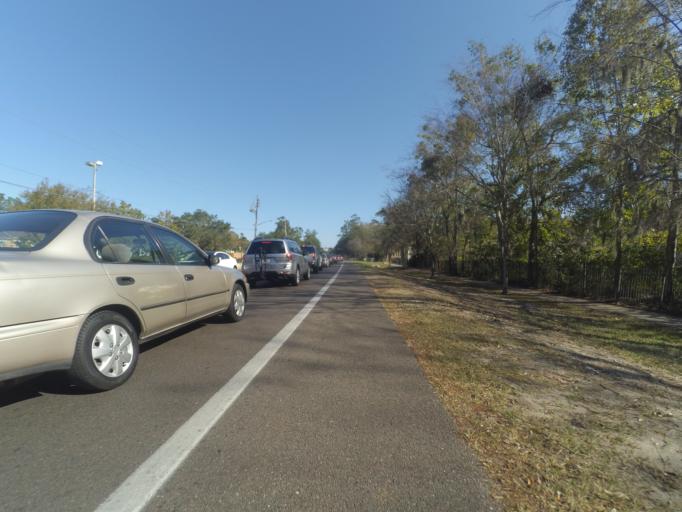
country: US
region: Florida
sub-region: Alachua County
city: Gainesville
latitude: 29.6340
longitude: -82.3830
